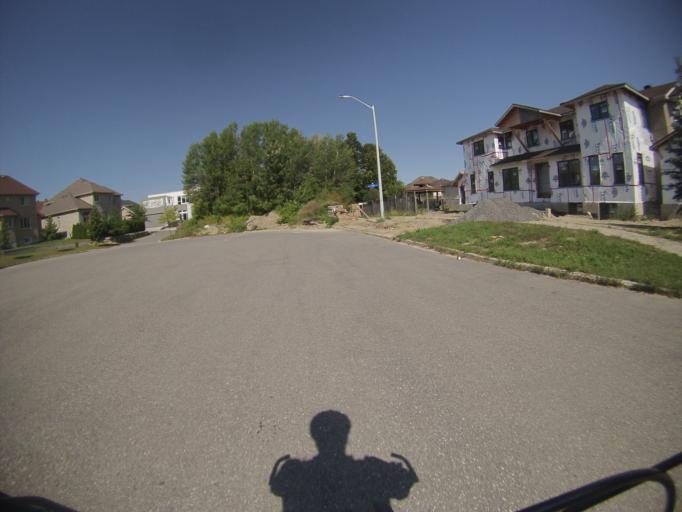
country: CA
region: Ontario
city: Ottawa
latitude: 45.3568
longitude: -75.6366
